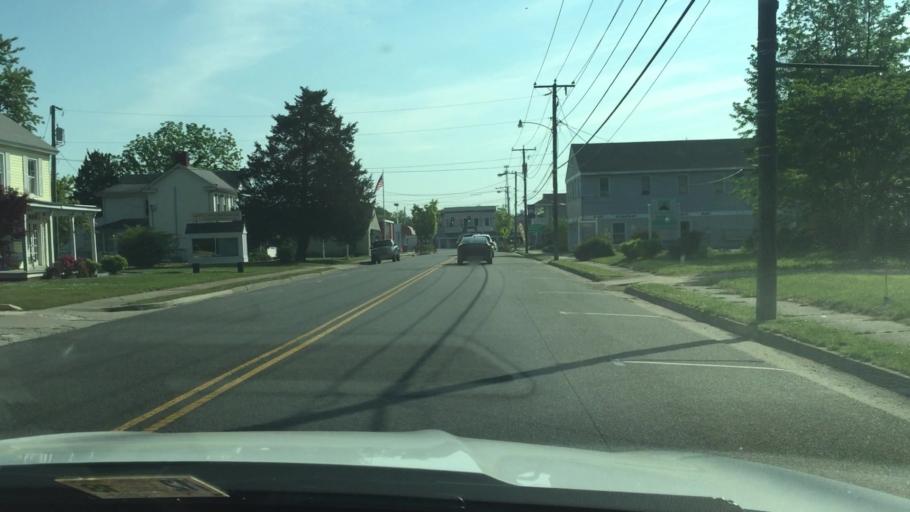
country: US
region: Virginia
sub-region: Lancaster County
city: Kilmarnock
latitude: 37.6476
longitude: -76.3910
